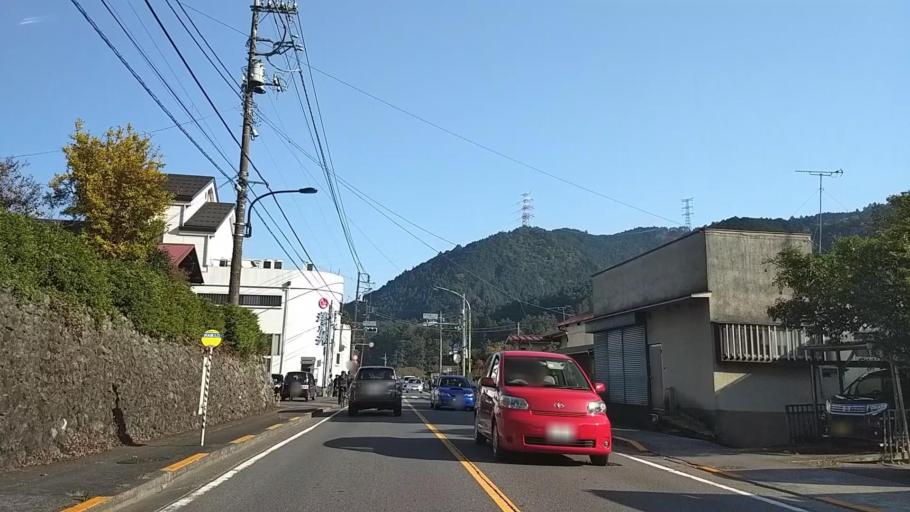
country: JP
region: Tokyo
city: Ome
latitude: 35.8048
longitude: 139.1927
